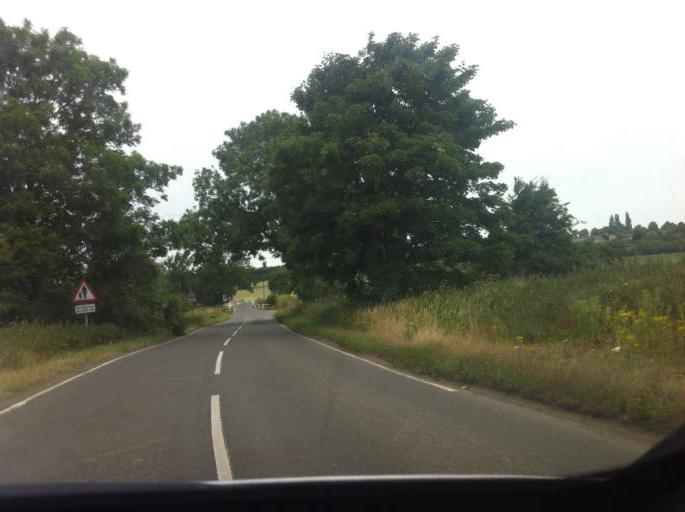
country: GB
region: England
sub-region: Northamptonshire
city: Earls Barton
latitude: 52.2634
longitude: -0.7144
